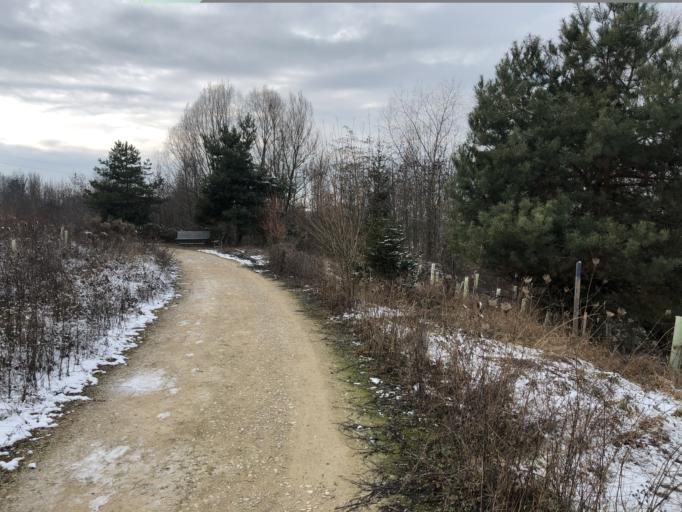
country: DE
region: Baden-Wuerttemberg
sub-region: Tuebingen Region
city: Nehren
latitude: 48.4182
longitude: 9.0750
